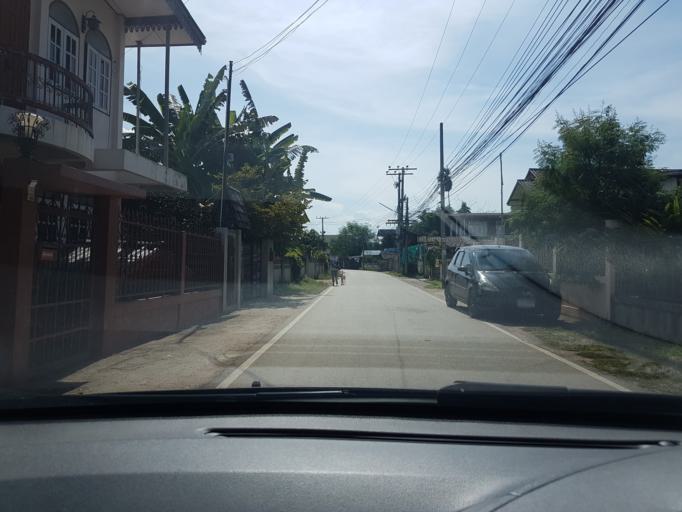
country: TH
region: Lampang
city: Ko Kha
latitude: 18.2211
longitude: 99.4135
